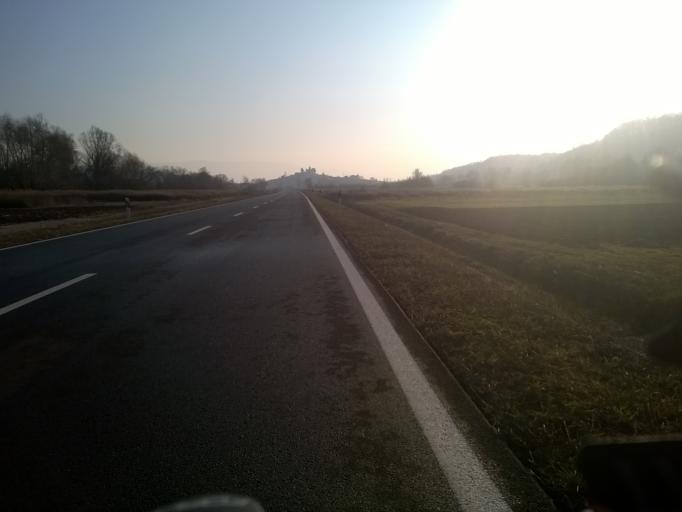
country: HR
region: Krapinsko-Zagorska
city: Zabok
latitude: 46.0525
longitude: 15.9129
